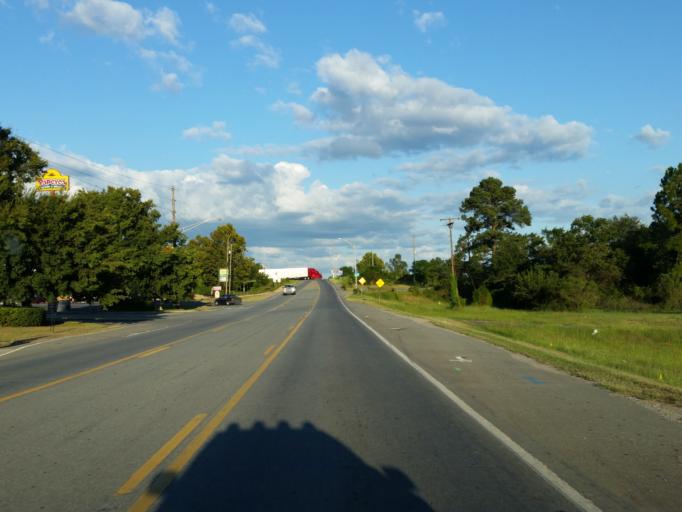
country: US
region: Georgia
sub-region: Dooly County
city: Vienna
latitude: 32.0867
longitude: -83.7665
